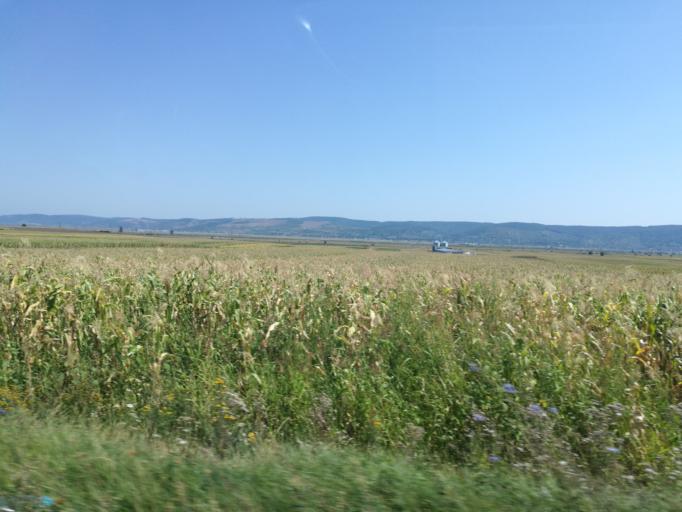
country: RO
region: Bacau
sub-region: Comuna Cleja
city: Somusca
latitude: 46.4156
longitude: 26.9357
